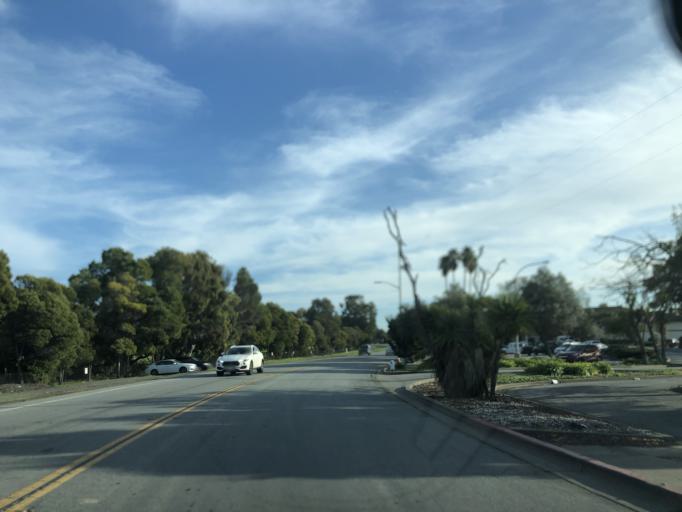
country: US
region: California
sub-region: Alameda County
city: San Leandro
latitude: 37.6991
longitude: -122.1890
